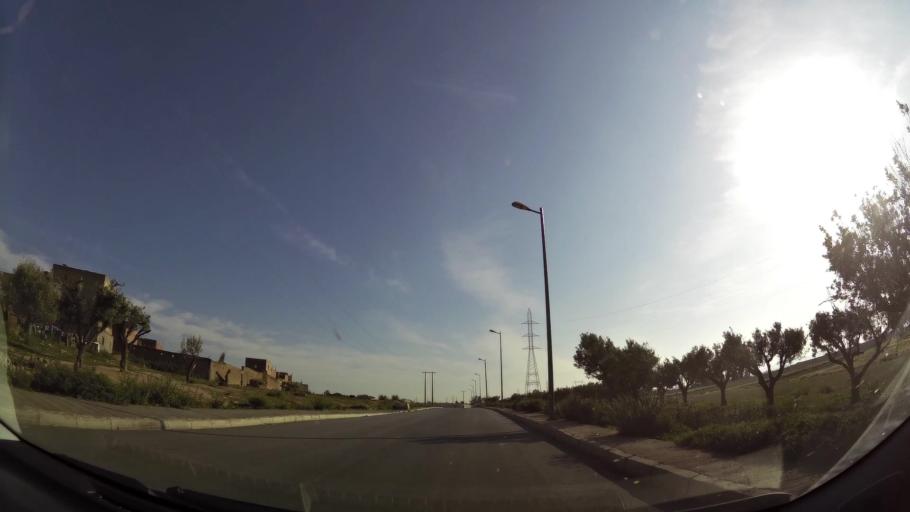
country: MA
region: Oriental
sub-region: Oujda-Angad
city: Oujda
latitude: 34.7178
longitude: -1.9070
